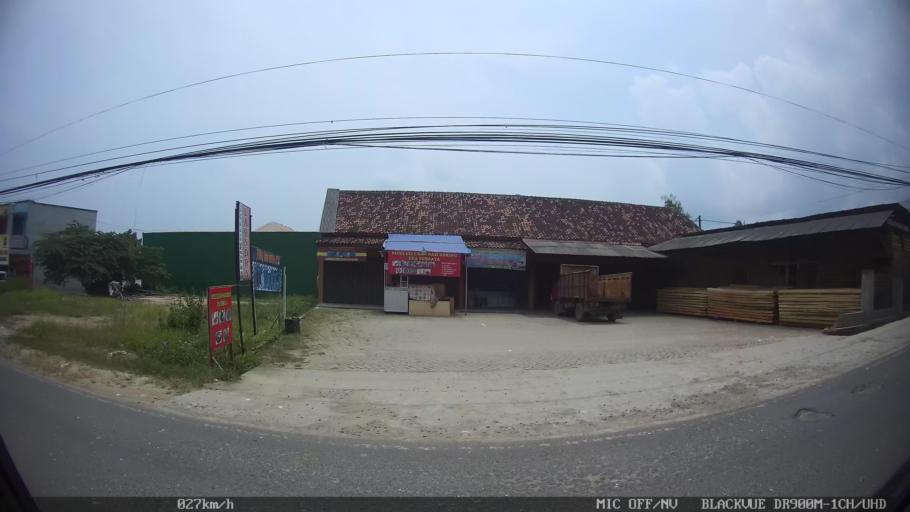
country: ID
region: Lampung
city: Kedaton
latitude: -5.4014
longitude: 105.3135
